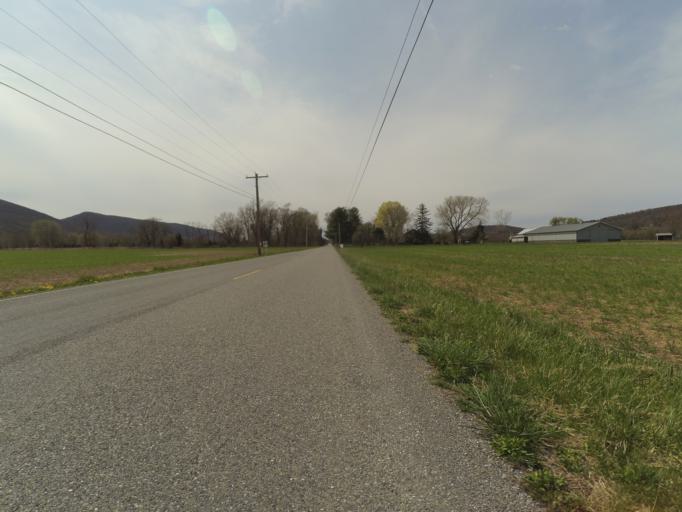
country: US
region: Pennsylvania
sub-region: Clinton County
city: Dunnstown
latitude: 41.1414
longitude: -77.4042
